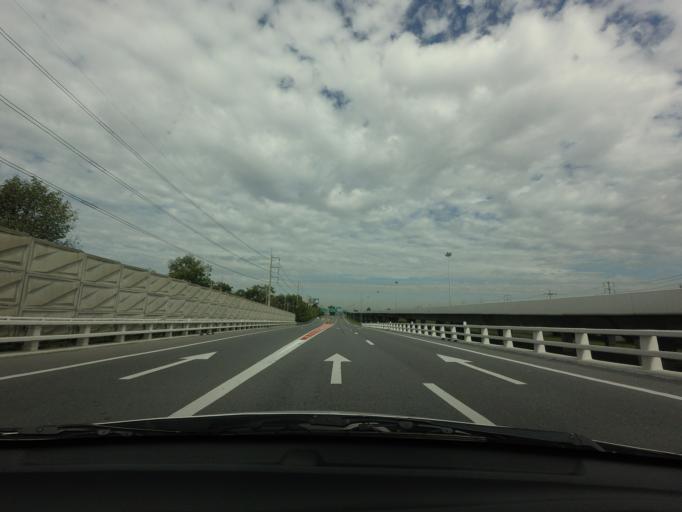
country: TH
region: Pathum Thani
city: Thanyaburi
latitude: 14.0019
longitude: 100.7072
